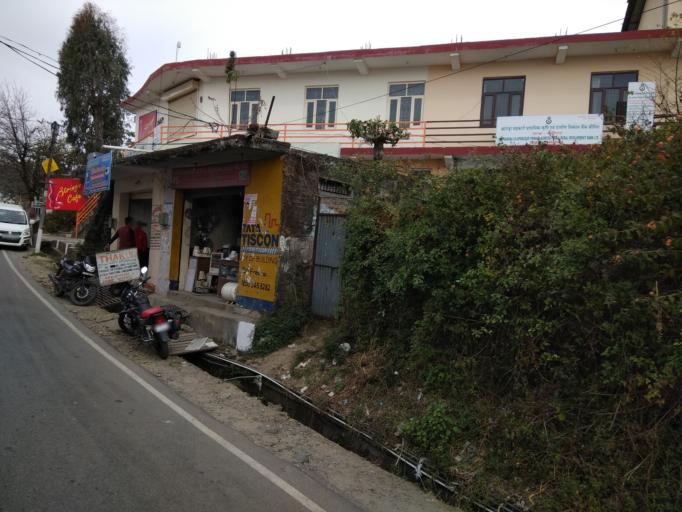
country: IN
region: Himachal Pradesh
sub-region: Kangra
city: Dharmsala
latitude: 32.2039
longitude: 76.3303
